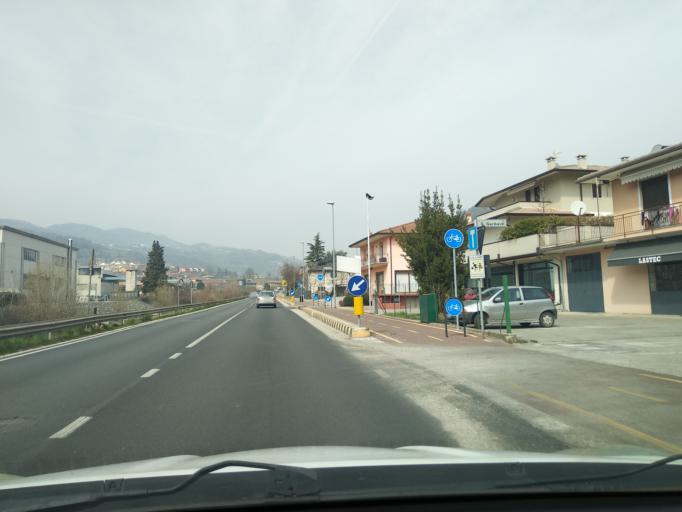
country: IT
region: Veneto
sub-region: Provincia di Vicenza
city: Chiampo
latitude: 45.5518
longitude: 11.2750
